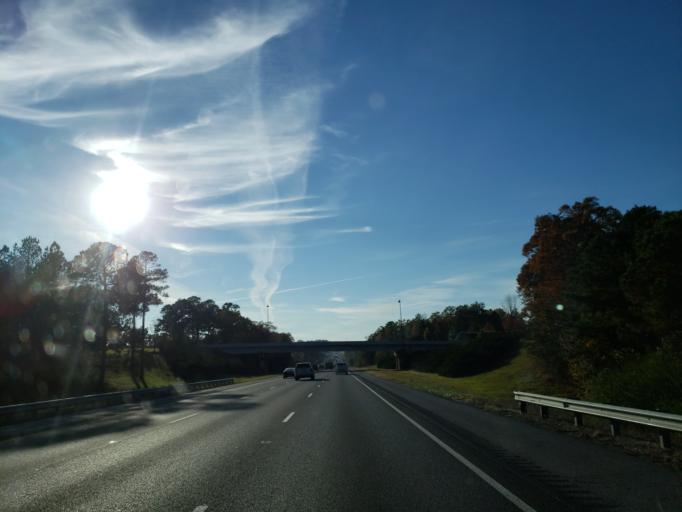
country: US
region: Alabama
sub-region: Tuscaloosa County
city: Vance
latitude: 33.1938
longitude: -87.2483
